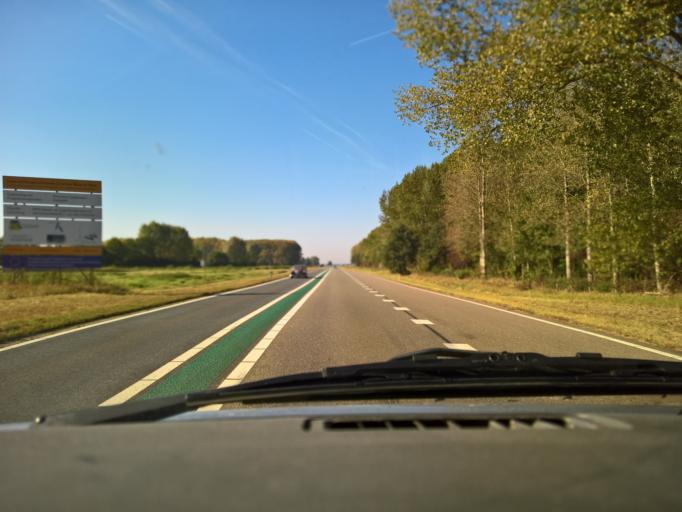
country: NL
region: Gelderland
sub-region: Gemeente Druten
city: Druten
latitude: 51.8696
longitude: 5.6066
